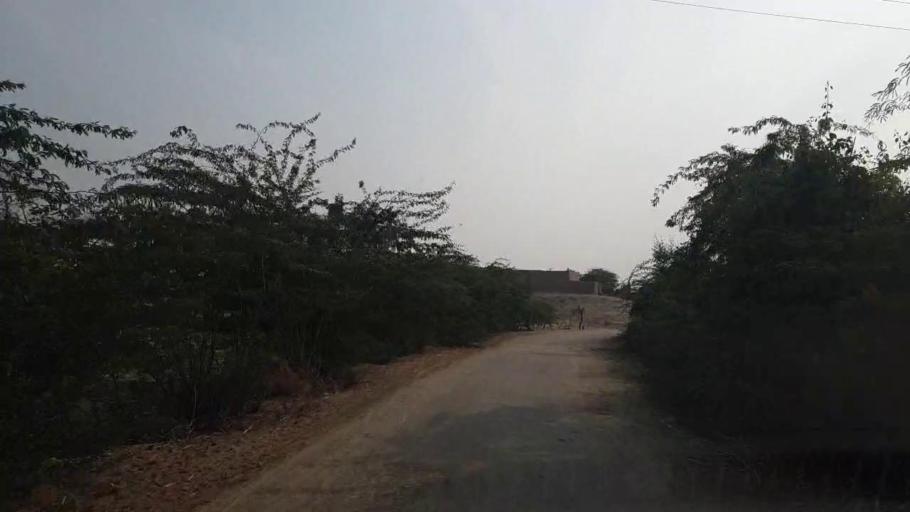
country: PK
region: Sindh
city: Sann
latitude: 26.0571
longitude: 68.1020
